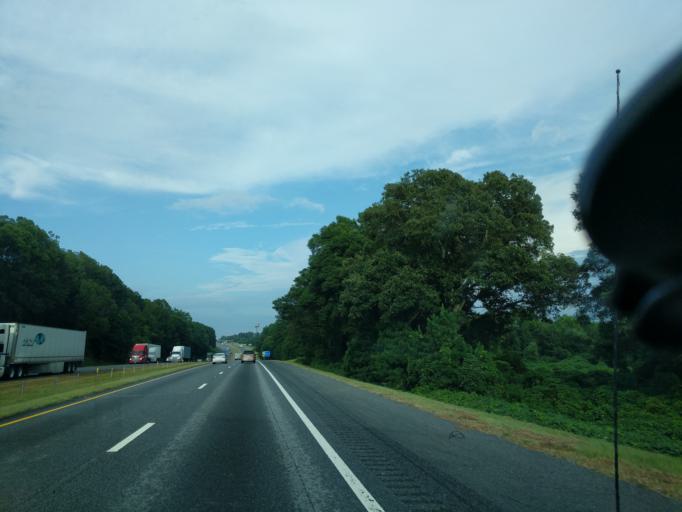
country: US
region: Georgia
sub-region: Hart County
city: Reed Creek
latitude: 34.5033
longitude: -82.9769
